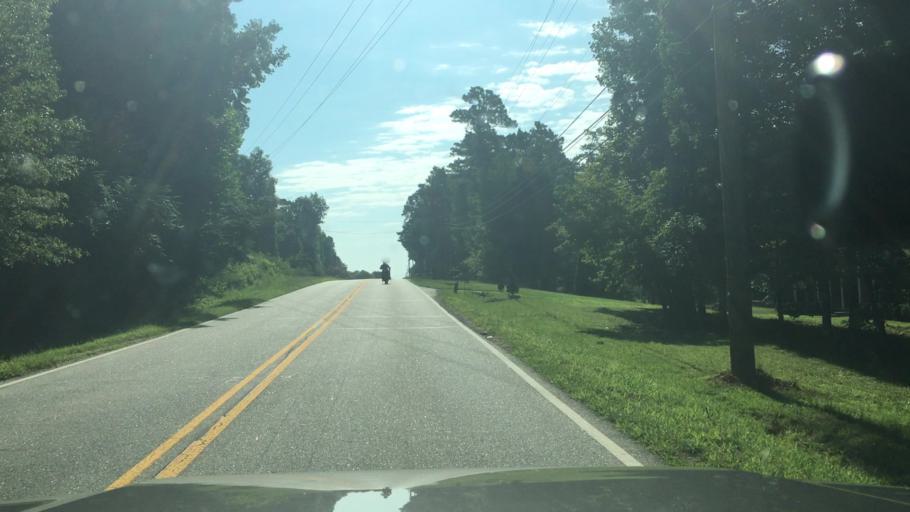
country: US
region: Georgia
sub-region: Coweta County
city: East Newnan
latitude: 33.3559
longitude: -84.7205
